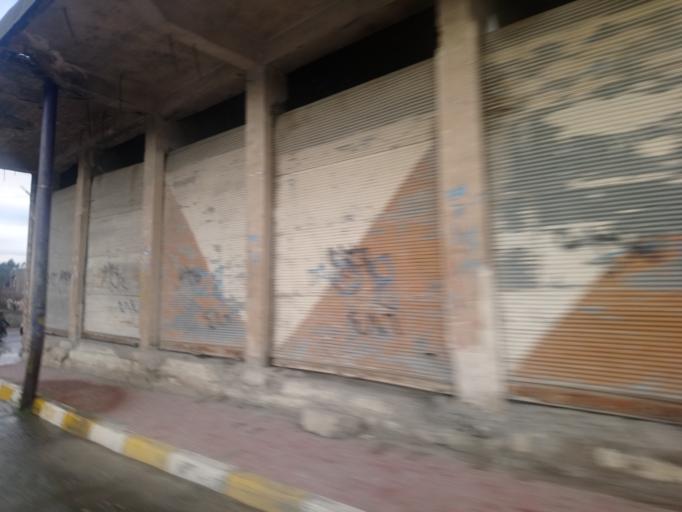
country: IQ
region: As Sulaymaniyah
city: Qeladize
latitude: 36.1854
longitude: 45.1167
